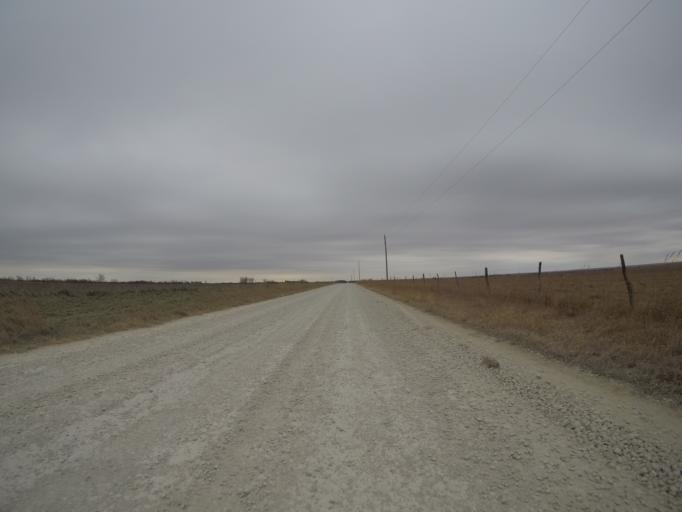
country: US
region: Kansas
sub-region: Wabaunsee County
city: Alma
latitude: 38.8240
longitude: -96.1133
